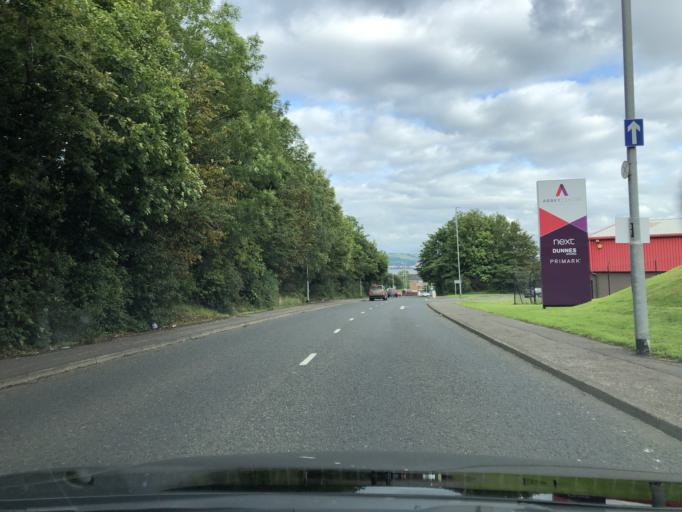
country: GB
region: Northern Ireland
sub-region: Newtownabbey District
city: Newtownabbey
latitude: 54.6558
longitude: -5.9152
